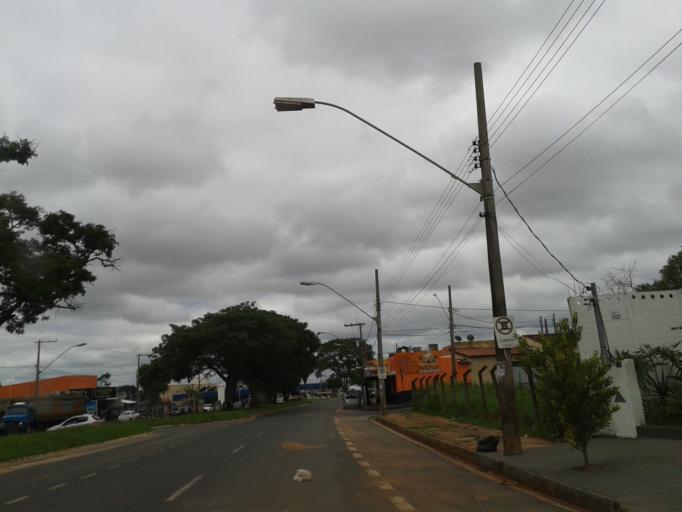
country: BR
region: Minas Gerais
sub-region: Uberlandia
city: Uberlandia
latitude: -18.9384
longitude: -48.2275
